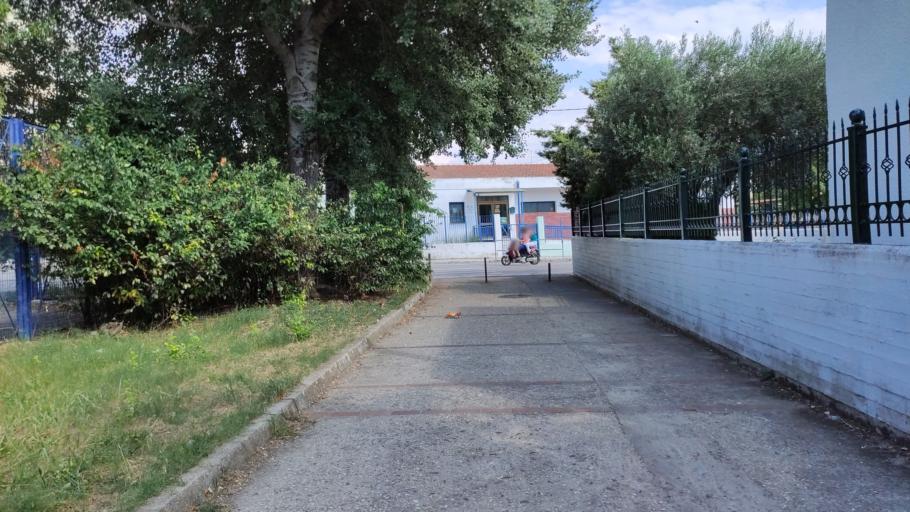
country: GR
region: East Macedonia and Thrace
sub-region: Nomos Rodopis
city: Komotini
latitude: 41.1220
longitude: 25.3926
